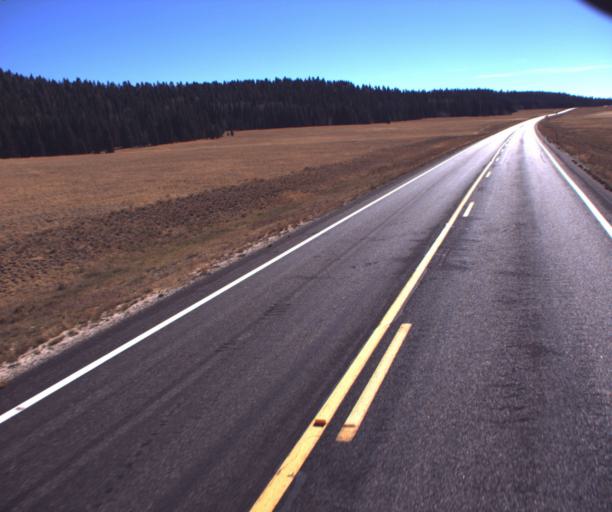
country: US
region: Arizona
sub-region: Coconino County
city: Grand Canyon
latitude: 36.3668
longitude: -112.1210
